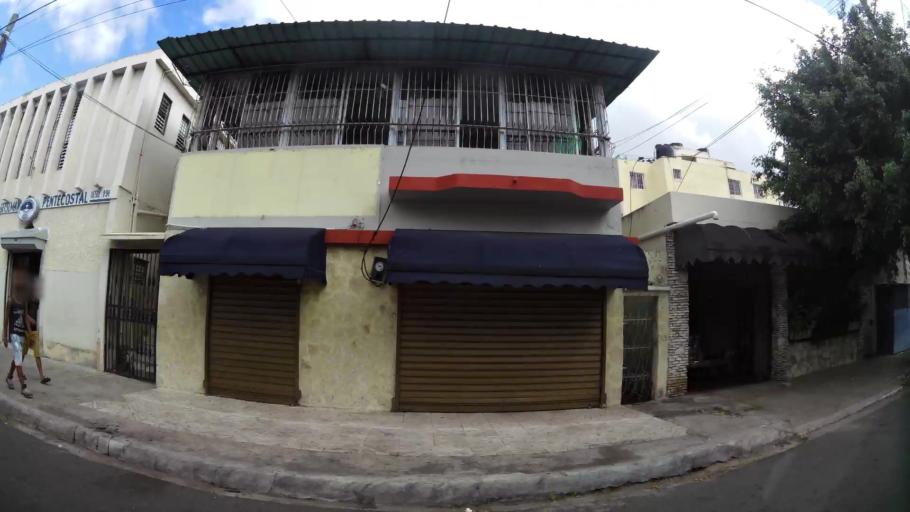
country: DO
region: Nacional
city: San Carlos
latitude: 18.4824
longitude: -69.9007
